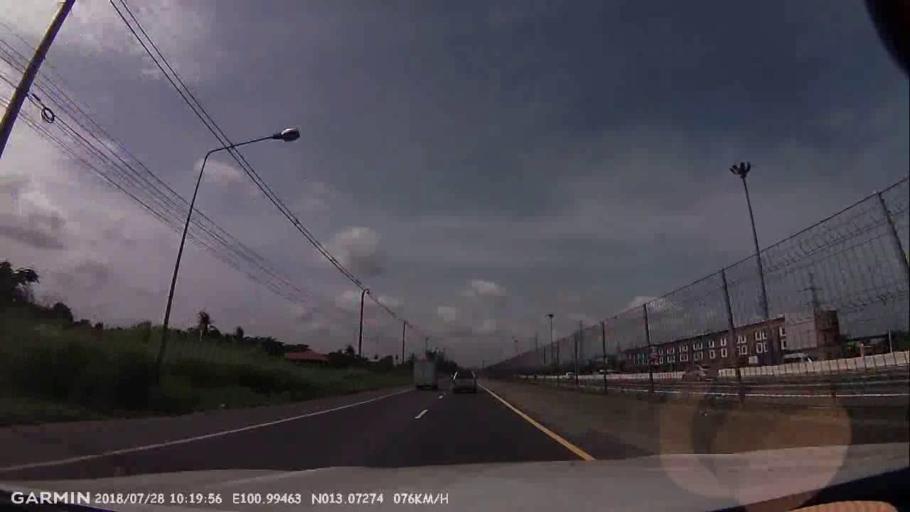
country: TH
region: Chon Buri
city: Ban Talat Bueng
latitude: 13.0725
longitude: 100.9947
